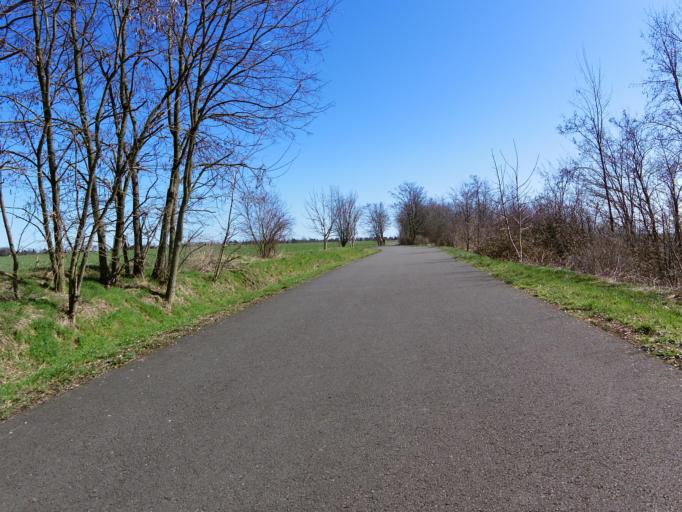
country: DE
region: Saxony
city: Markkleeberg
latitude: 51.2709
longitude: 12.4132
